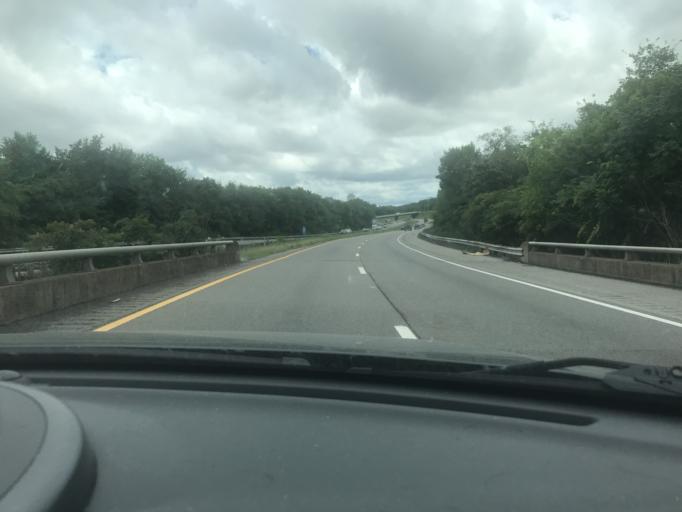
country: US
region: Tennessee
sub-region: Davidson County
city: Nashville
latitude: 36.1888
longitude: -86.7544
